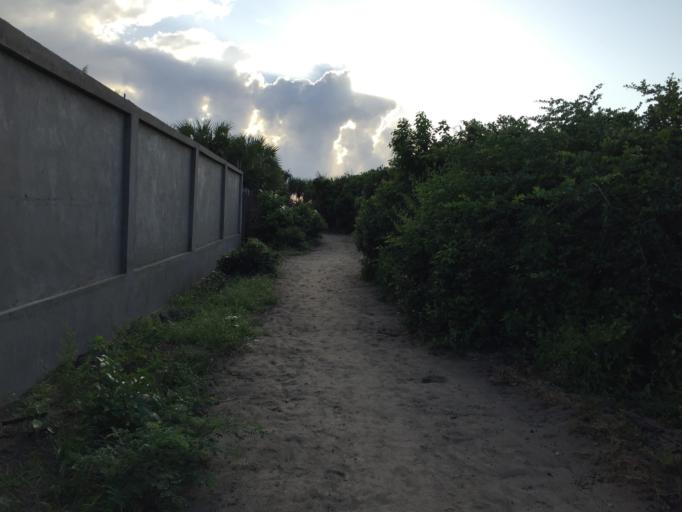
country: TZ
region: Pwani
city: Vikindu
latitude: -7.0156
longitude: 39.5487
